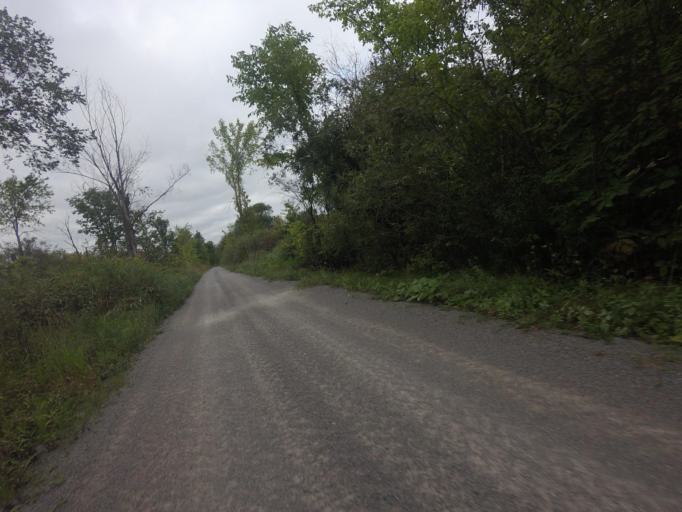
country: CA
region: Ontario
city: Omemee
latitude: 44.4458
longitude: -78.7687
